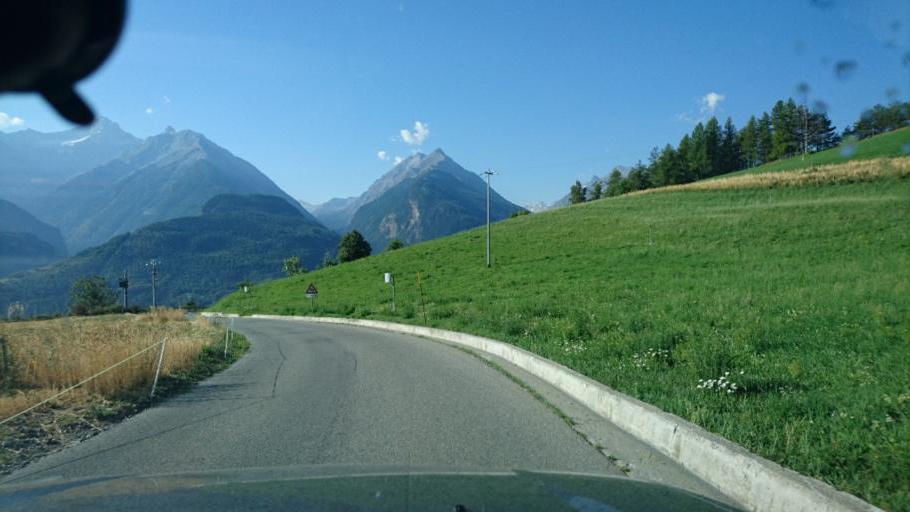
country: IT
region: Aosta Valley
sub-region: Valle d'Aosta
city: Villeneuve
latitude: 45.7184
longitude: 7.2067
